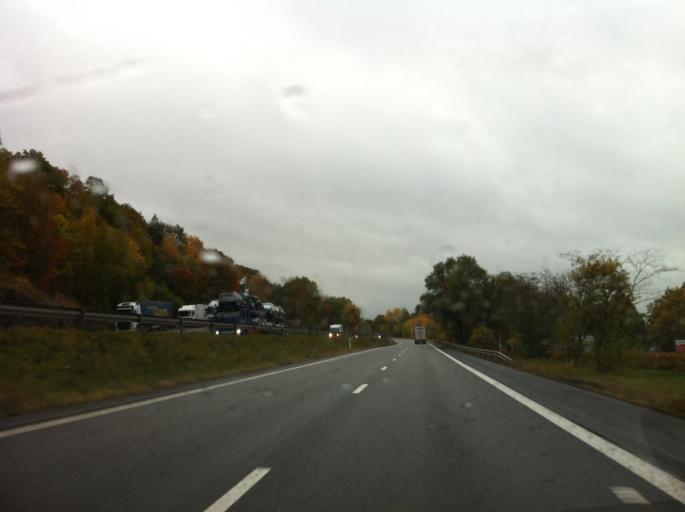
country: SE
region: Joenkoeping
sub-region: Jonkopings Kommun
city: Kaxholmen
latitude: 57.8548
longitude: 14.2668
